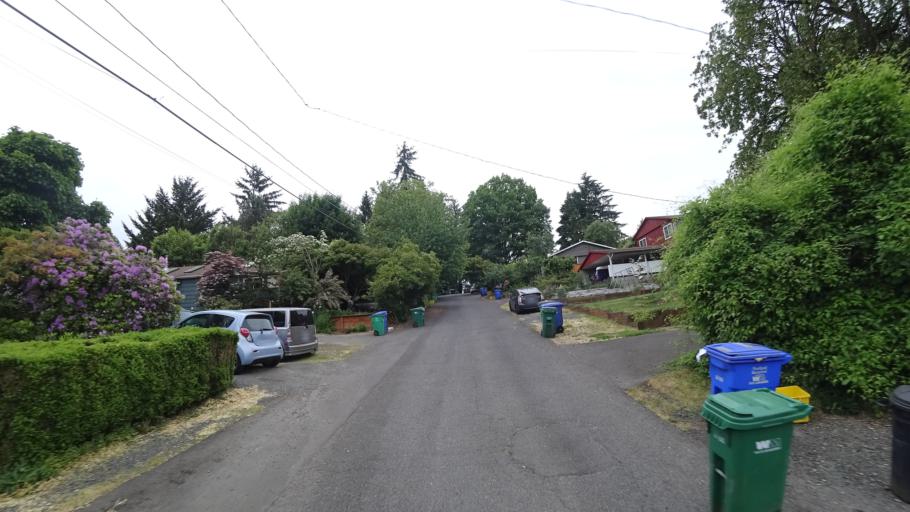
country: US
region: Oregon
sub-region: Clackamas County
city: Lake Oswego
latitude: 45.4586
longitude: -122.6789
